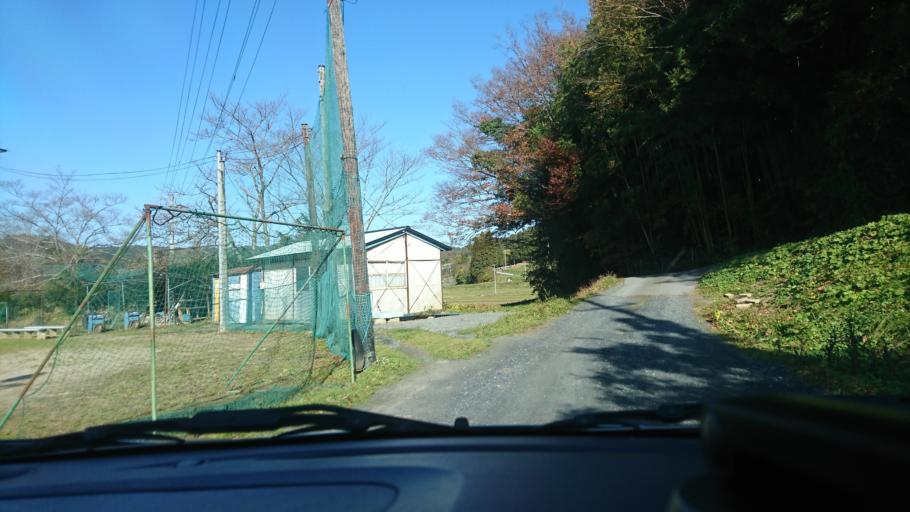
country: JP
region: Iwate
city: Ichinoseki
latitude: 38.8521
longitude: 141.2886
